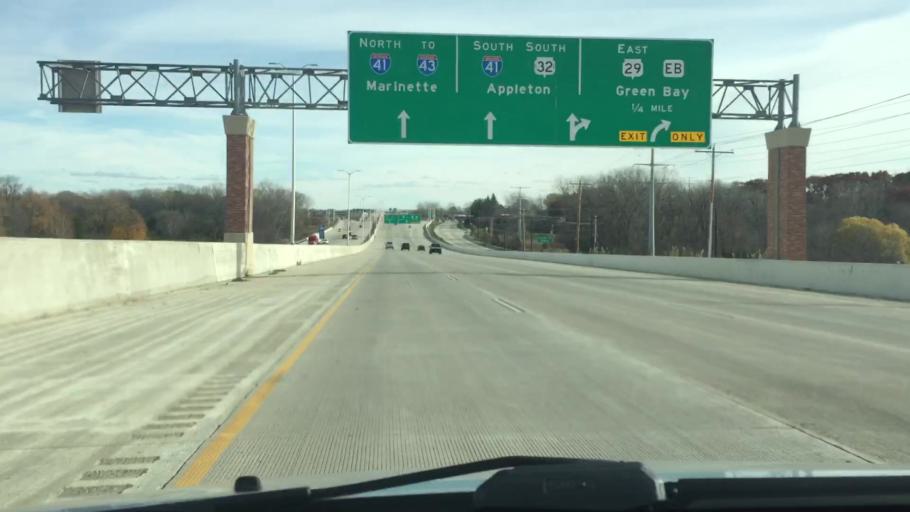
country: US
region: Wisconsin
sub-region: Brown County
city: Howard
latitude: 44.5476
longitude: -88.0995
